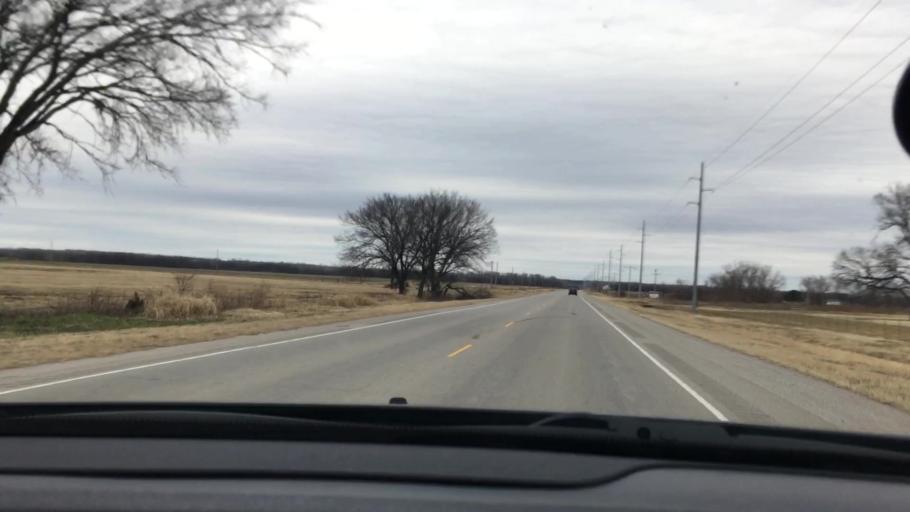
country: US
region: Oklahoma
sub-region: Marshall County
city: Oakland
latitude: 34.1990
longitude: -96.8022
